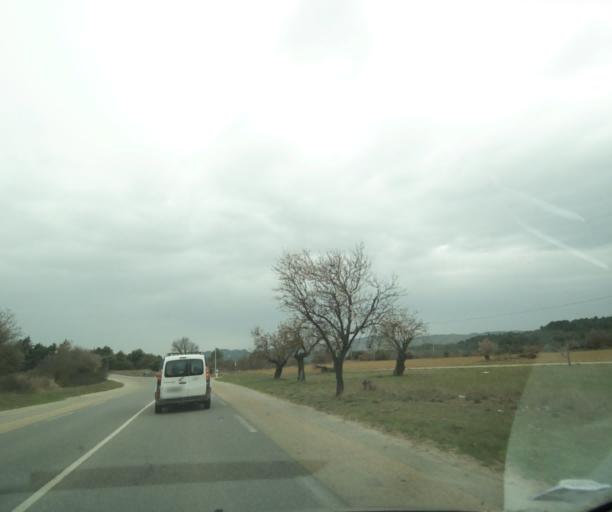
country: FR
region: Provence-Alpes-Cote d'Azur
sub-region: Departement des Bouches-du-Rhone
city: Jouques
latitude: 43.6406
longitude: 5.6142
